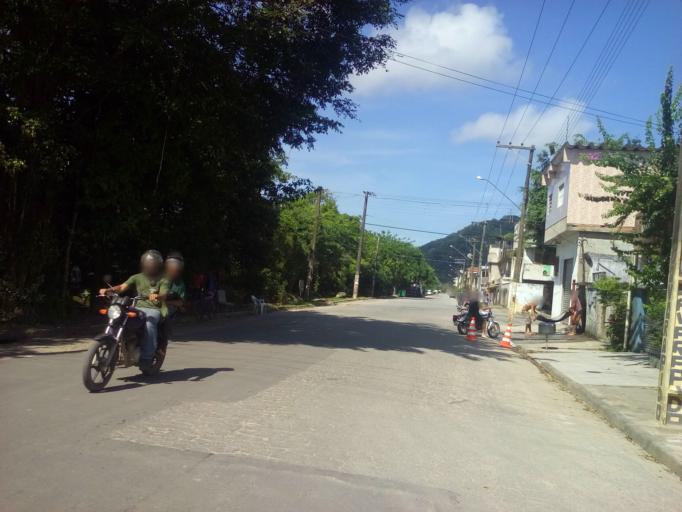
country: BR
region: Sao Paulo
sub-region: Guaruja
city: Guaruja
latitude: -23.9597
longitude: -46.2514
